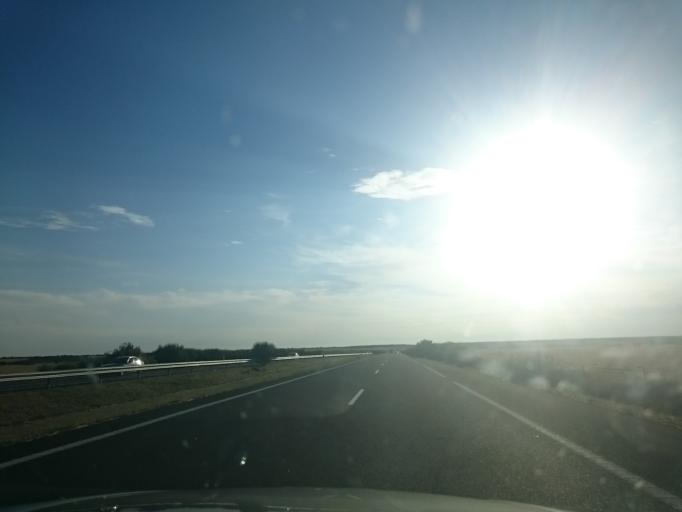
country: ES
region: Castille and Leon
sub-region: Provincia de Palencia
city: Ledigos
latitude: 42.3584
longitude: -4.8033
